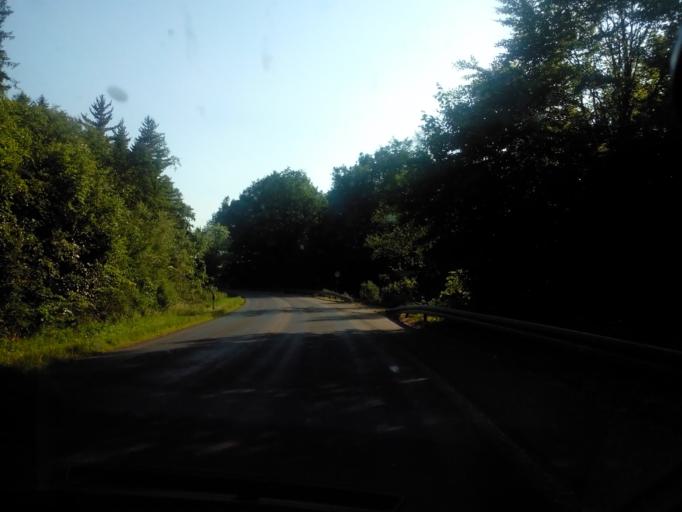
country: DE
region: Saarland
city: Beckingen
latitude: 49.4027
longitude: 6.7185
